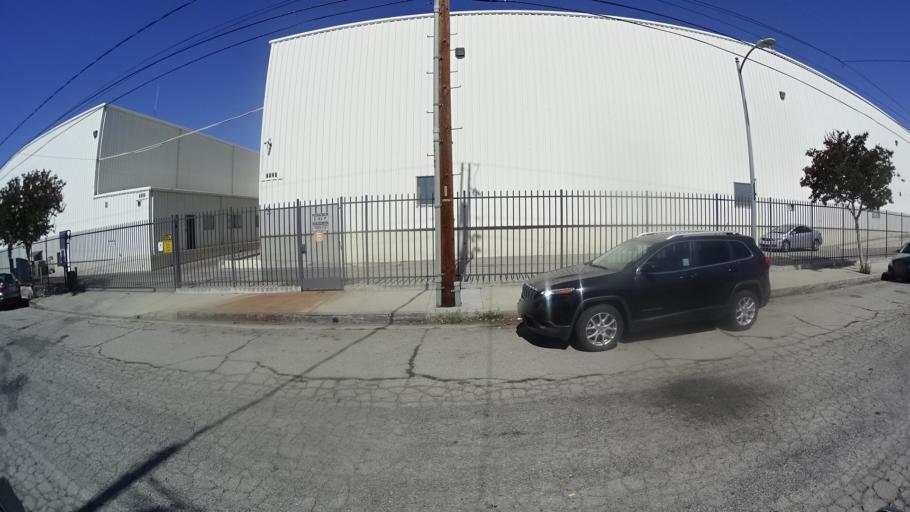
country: US
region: California
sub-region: Los Angeles County
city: Van Nuys
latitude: 34.1995
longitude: -118.4870
